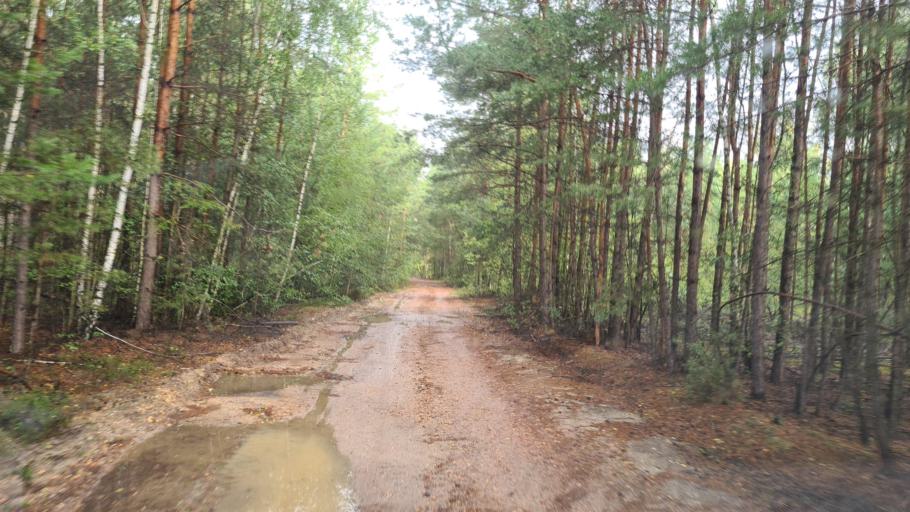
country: DE
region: Brandenburg
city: Sallgast
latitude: 51.5884
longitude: 13.8005
